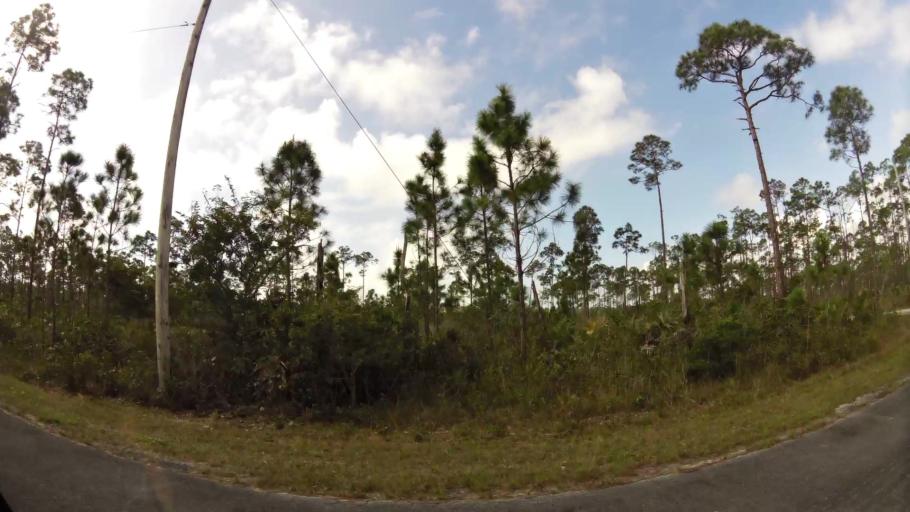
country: BS
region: Freeport
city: Lucaya
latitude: 26.5841
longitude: -78.5482
